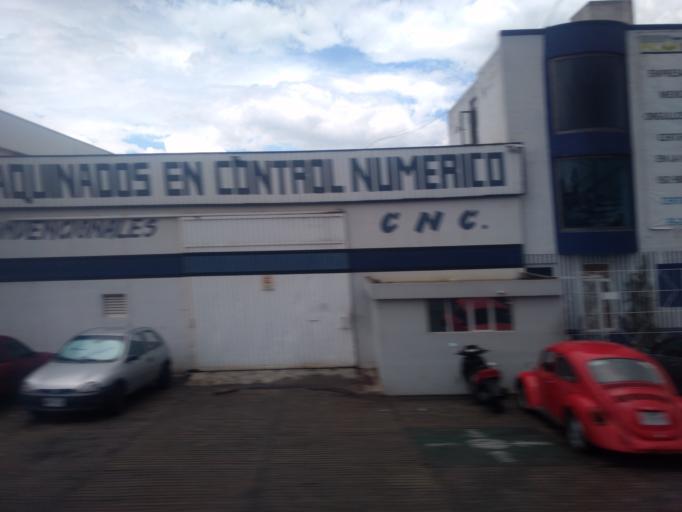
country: MX
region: Tlaxcala
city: Seccion Primera Santiago Tetla
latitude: 19.4395
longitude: -98.1304
